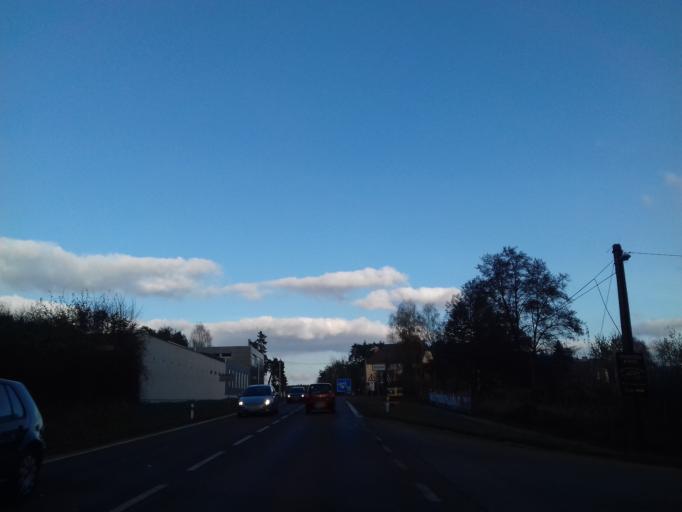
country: CZ
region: Plzensky
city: Line
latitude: 49.7056
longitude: 13.2758
